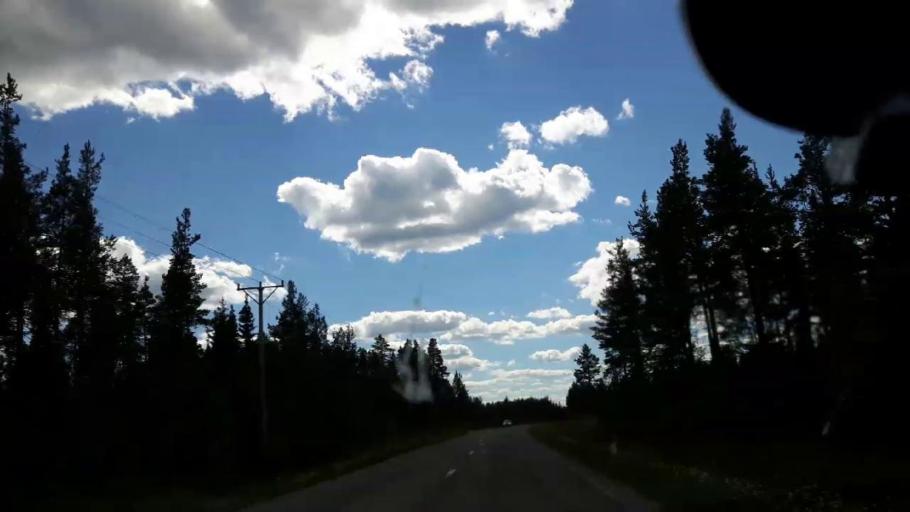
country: SE
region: Jaemtland
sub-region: Ragunda Kommun
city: Hammarstrand
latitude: 63.0035
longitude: 16.1144
